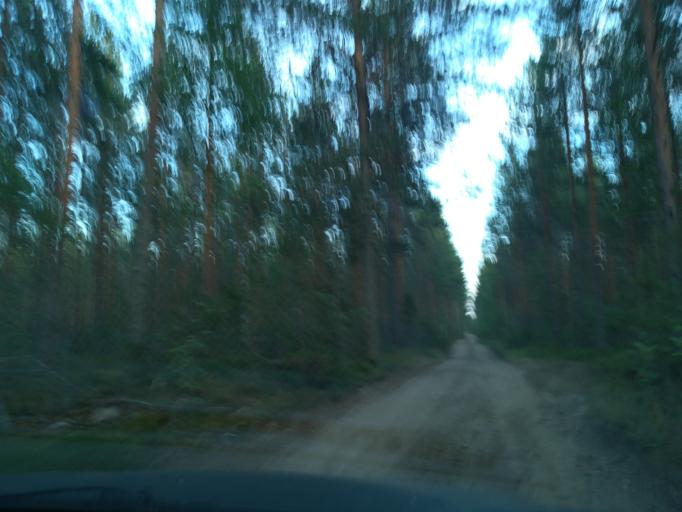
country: FI
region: South Karelia
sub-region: Lappeenranta
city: Joutseno
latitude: 61.3425
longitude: 28.4036
